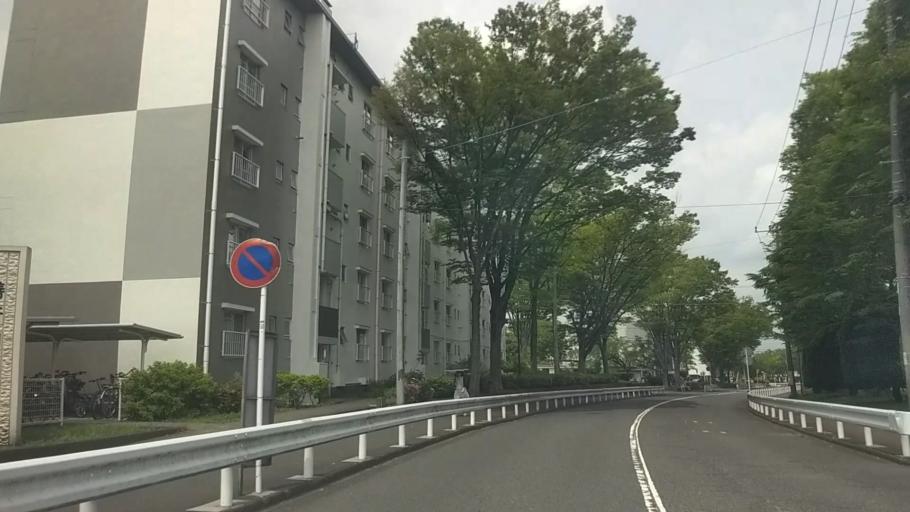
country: JP
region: Kanagawa
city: Fujisawa
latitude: 35.3658
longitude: 139.4676
